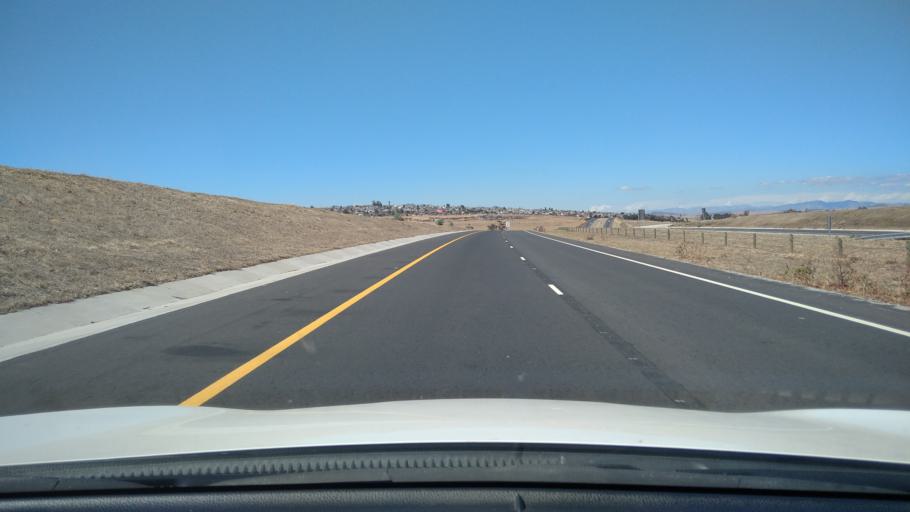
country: ZA
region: Western Cape
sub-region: West Coast District Municipality
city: Malmesbury
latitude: -33.4799
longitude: 18.6802
